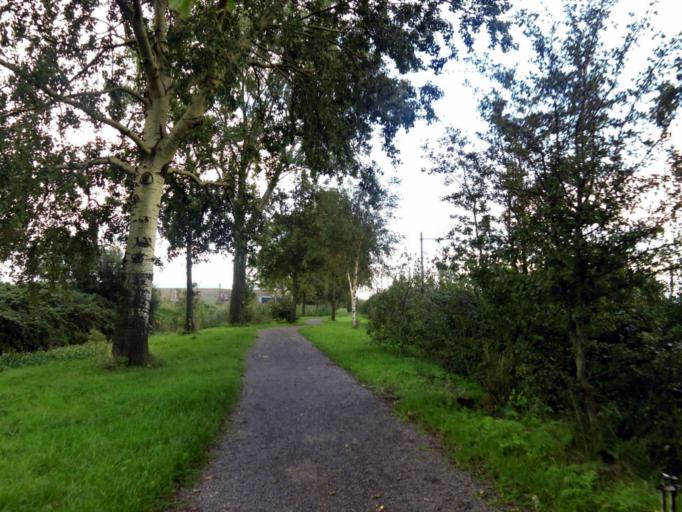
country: NL
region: South Holland
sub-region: Gemeente Leiderdorp
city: Leiderdorp
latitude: 52.1378
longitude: 4.5196
